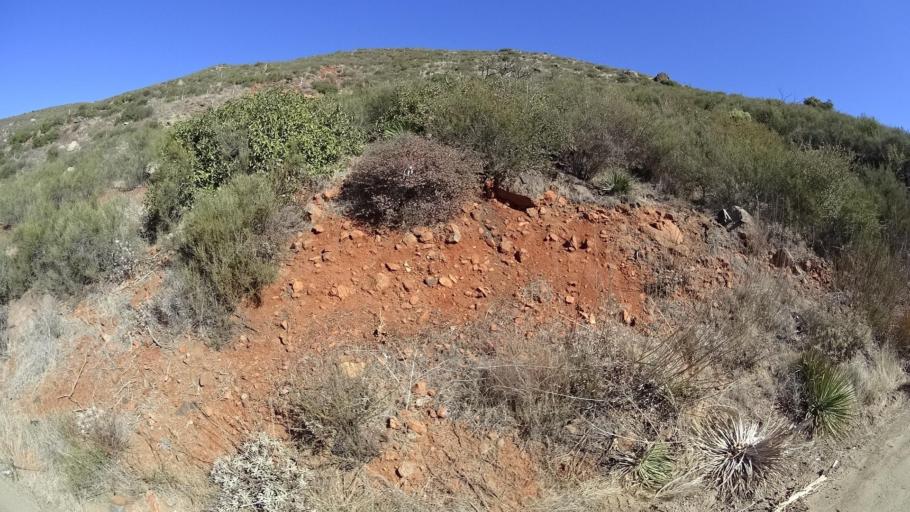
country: US
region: California
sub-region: San Diego County
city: Descanso
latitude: 32.8614
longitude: -116.6737
